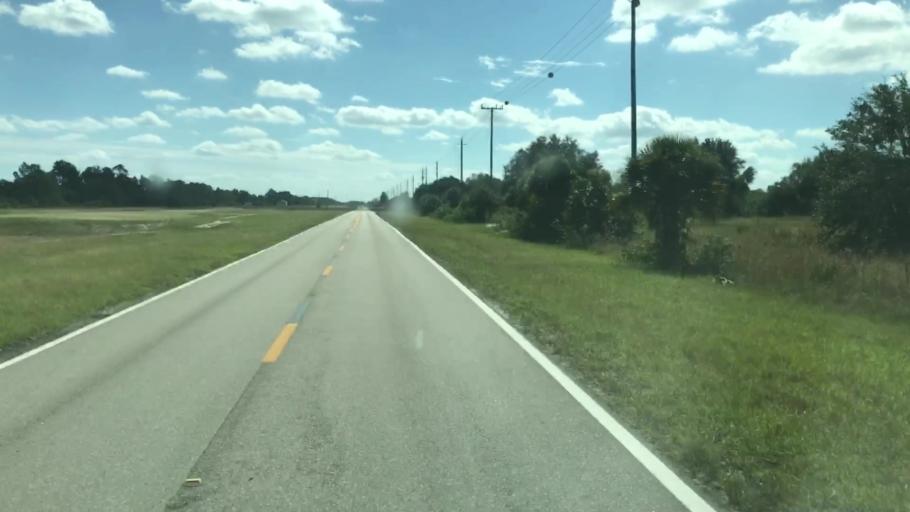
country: US
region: Florida
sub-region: Lee County
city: Lehigh Acres
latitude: 26.6718
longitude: -81.6637
